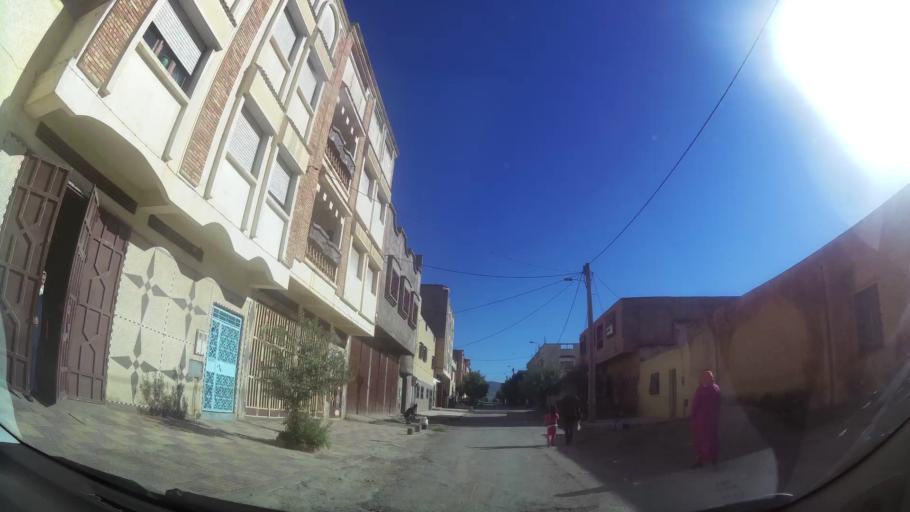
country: MA
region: Oriental
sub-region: Berkane-Taourirt
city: Ahfir
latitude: 34.9567
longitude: -2.0989
